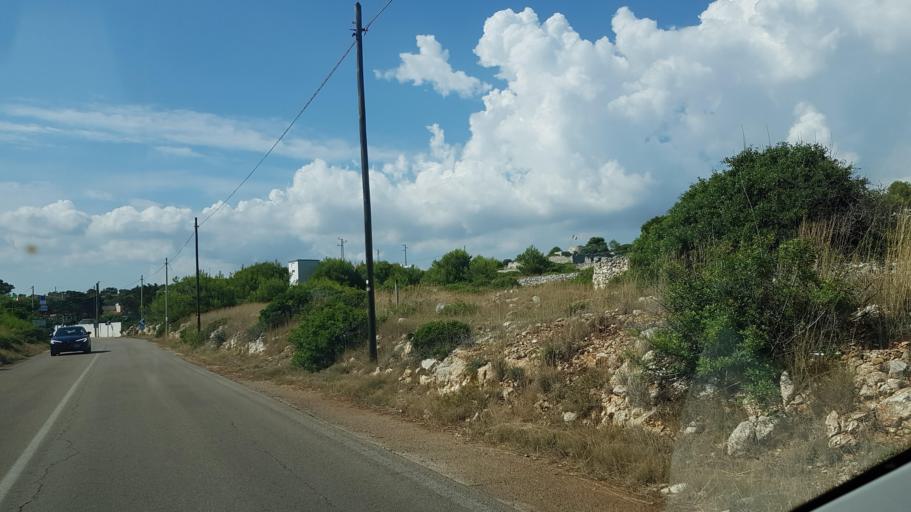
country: IT
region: Apulia
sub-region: Provincia di Lecce
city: Leuca
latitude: 39.7949
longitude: 18.3419
